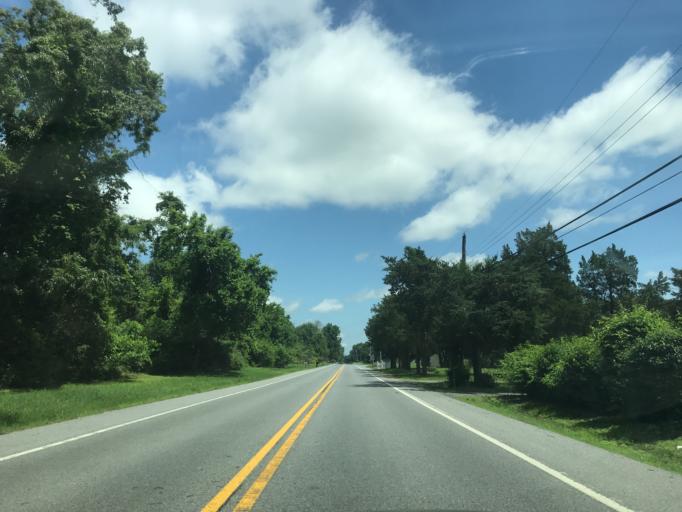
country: US
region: Maryland
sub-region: Caroline County
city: Federalsburg
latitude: 38.6976
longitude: -75.7630
